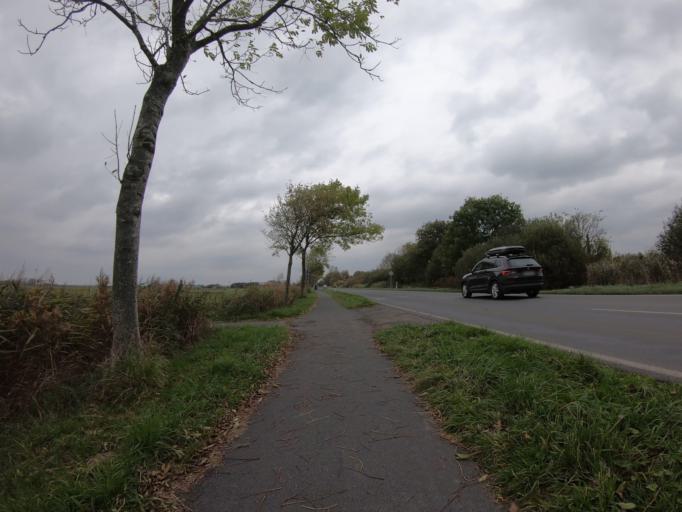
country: DE
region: Lower Saxony
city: Wirdum
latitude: 53.4861
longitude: 7.0625
